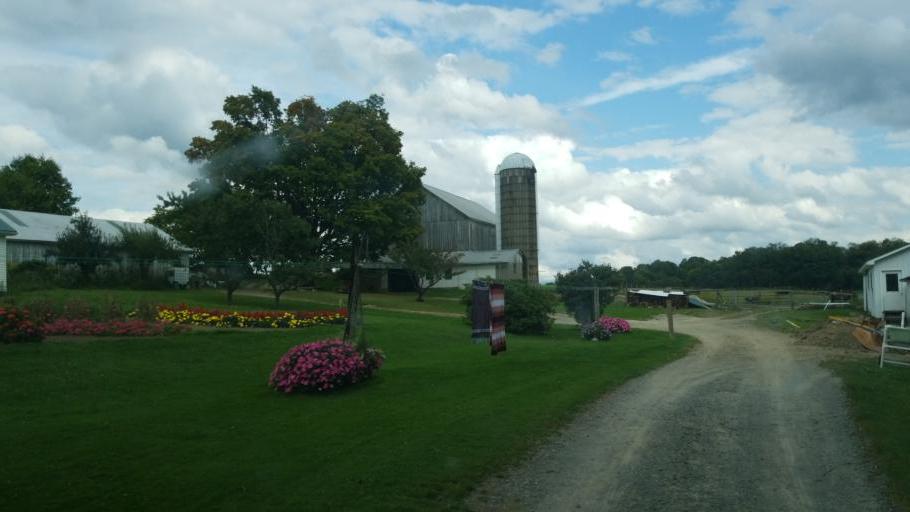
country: US
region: Pennsylvania
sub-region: Crawford County
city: Conneaut Lakeshore
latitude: 41.5357
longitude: -80.3152
